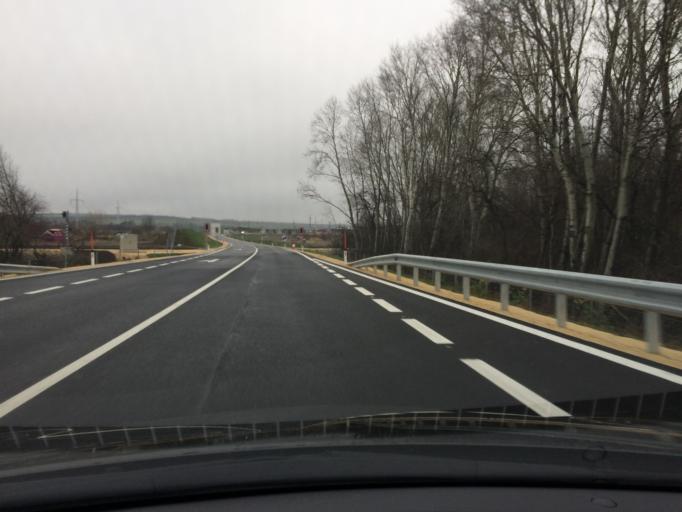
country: AT
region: Lower Austria
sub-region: Politischer Bezirk Mistelbach
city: Mistelbach
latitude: 48.5561
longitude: 16.5581
